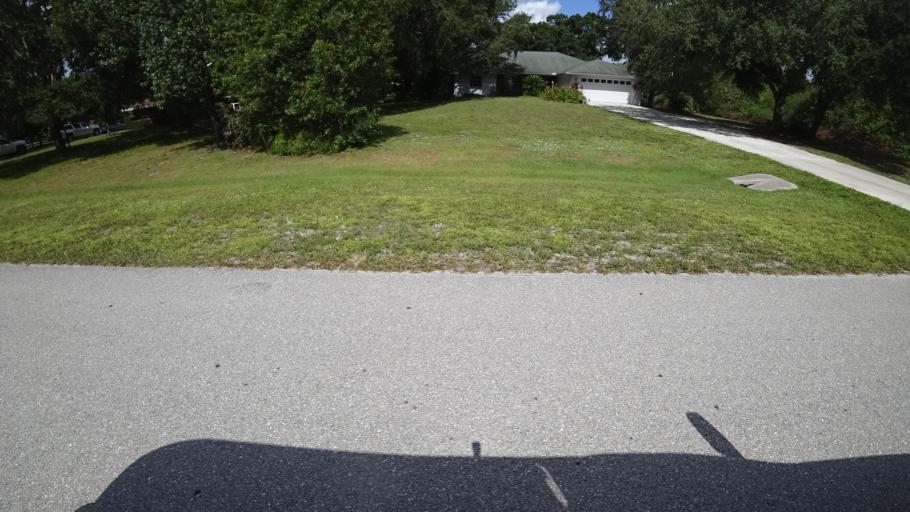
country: US
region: Florida
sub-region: Manatee County
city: Samoset
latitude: 27.4632
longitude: -82.4831
